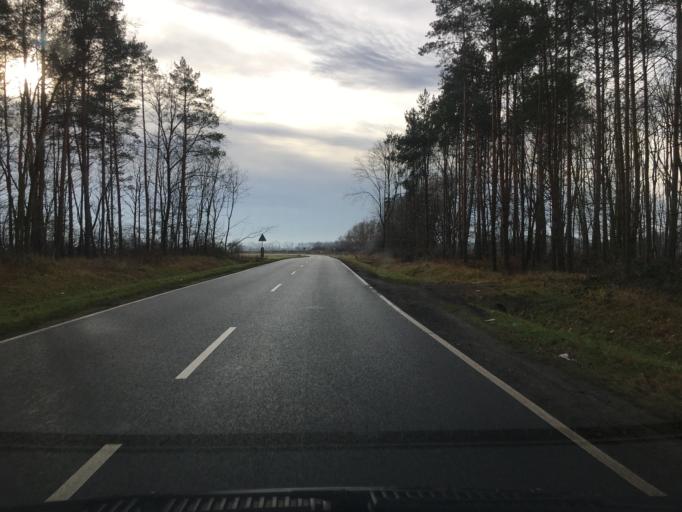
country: PL
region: Lower Silesian Voivodeship
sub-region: Powiat wroclawski
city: Dlugoleka
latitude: 51.1773
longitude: 17.2218
